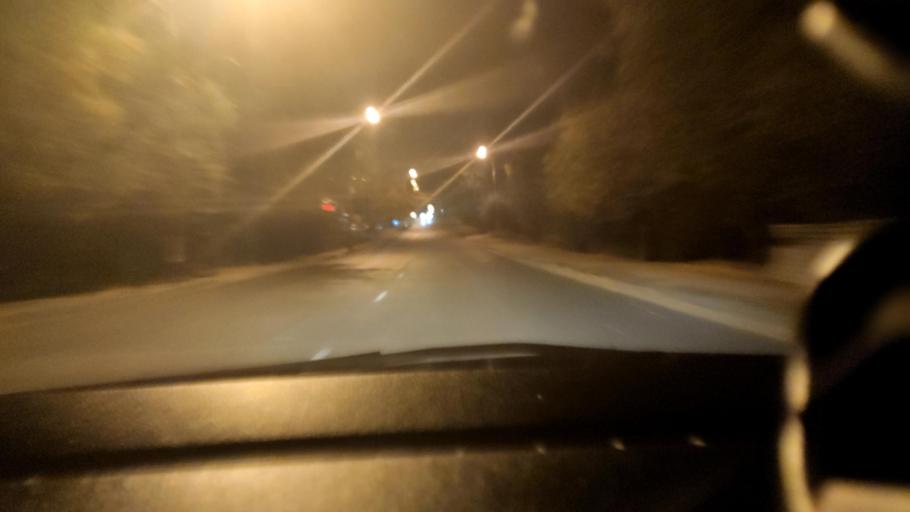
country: RU
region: Voronezj
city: Voronezh
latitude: 51.6932
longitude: 39.1646
